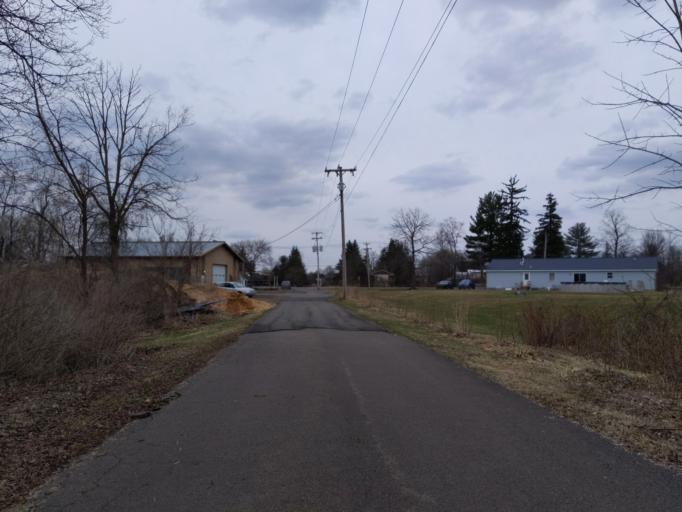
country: US
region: New York
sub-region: Tompkins County
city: Dryden
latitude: 42.5115
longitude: -76.3437
